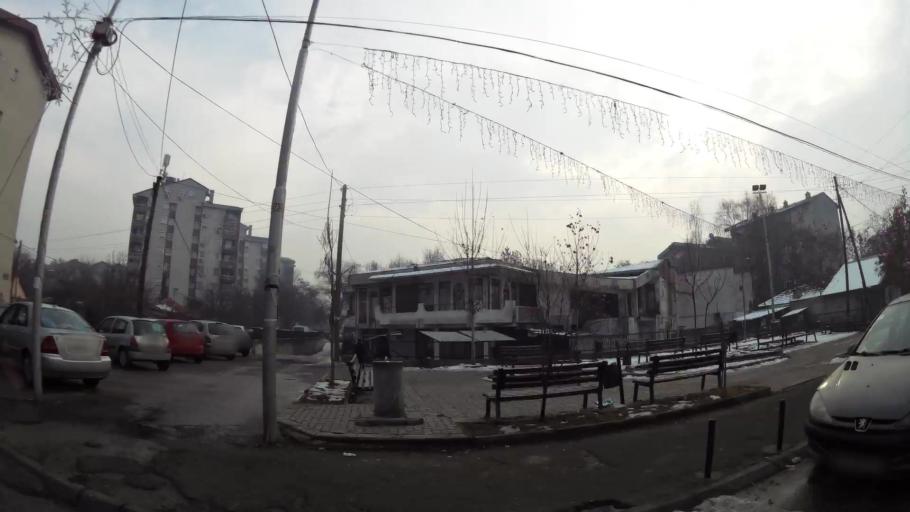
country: MK
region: Kisela Voda
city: Kisela Voda
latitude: 41.9957
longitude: 21.5095
